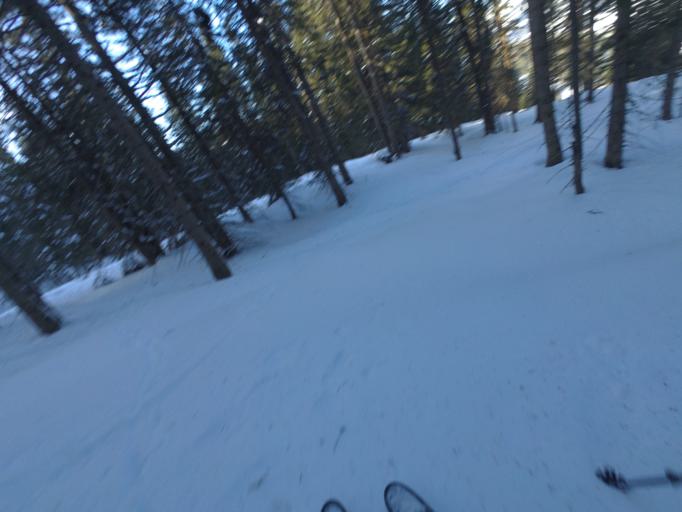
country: AT
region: Salzburg
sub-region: Politischer Bezirk Zell am See
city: Lend
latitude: 47.2708
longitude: 13.0189
